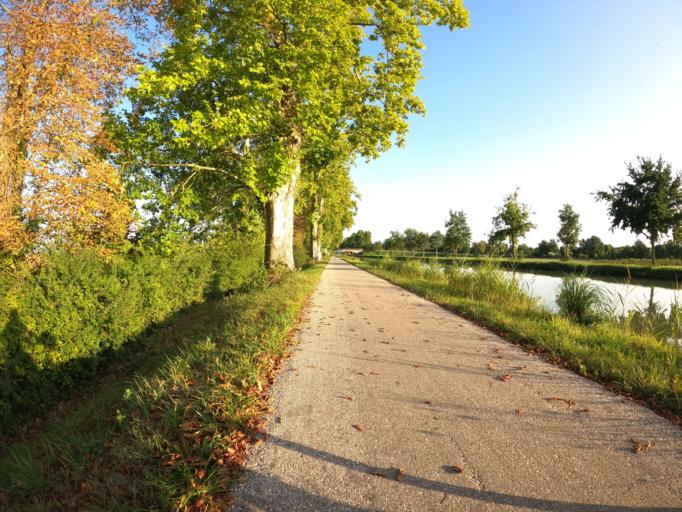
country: FR
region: Midi-Pyrenees
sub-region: Departement du Tarn-et-Garonne
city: Saint-Porquier
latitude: 44.0167
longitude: 1.1713
